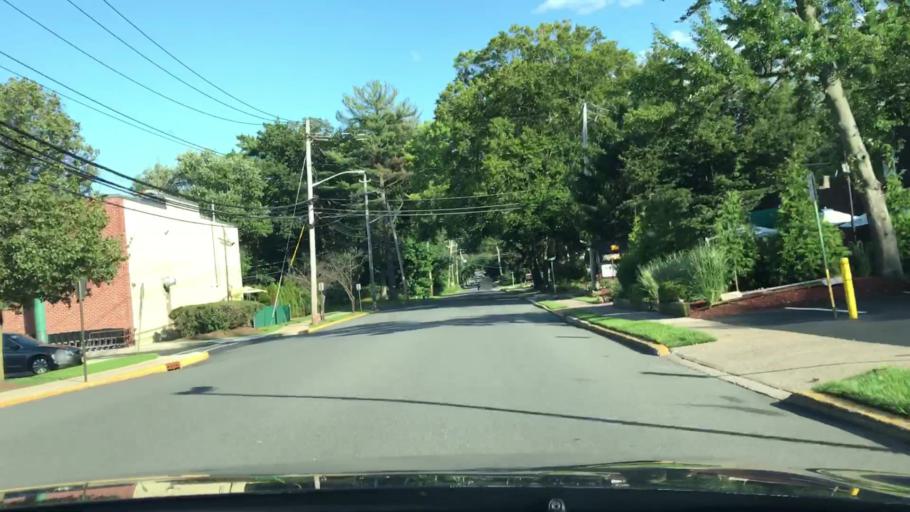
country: US
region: New Jersey
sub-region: Bergen County
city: Cresskill
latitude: 40.9408
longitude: -73.9612
